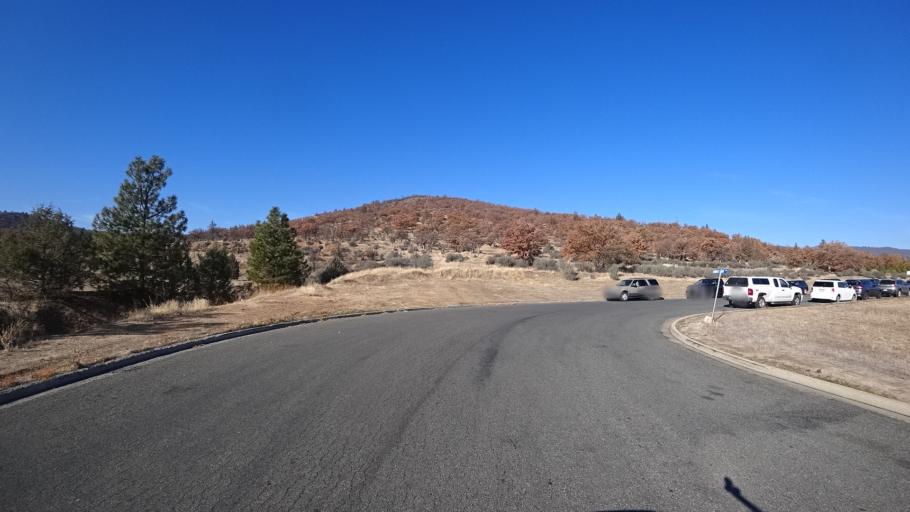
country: US
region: California
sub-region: Siskiyou County
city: Yreka
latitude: 41.7042
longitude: -122.6479
